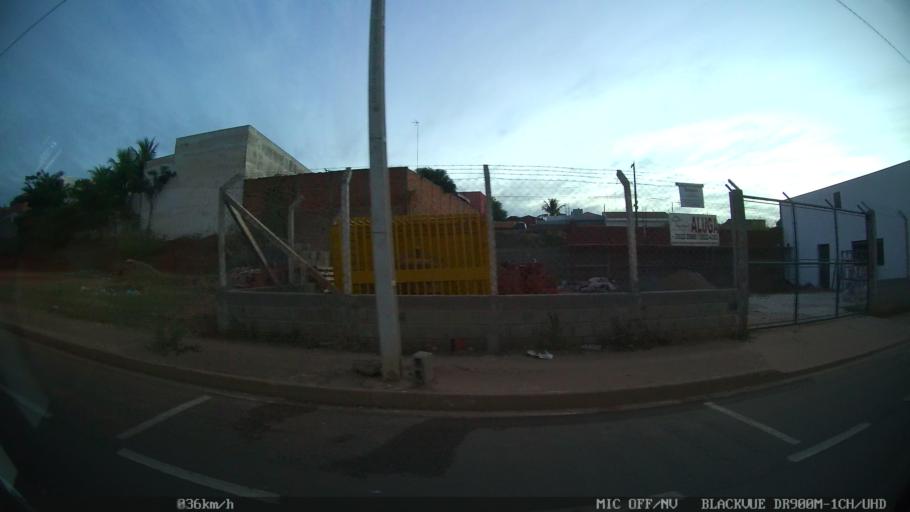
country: BR
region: Sao Paulo
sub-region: Catanduva
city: Catanduva
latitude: -21.1363
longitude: -48.9899
